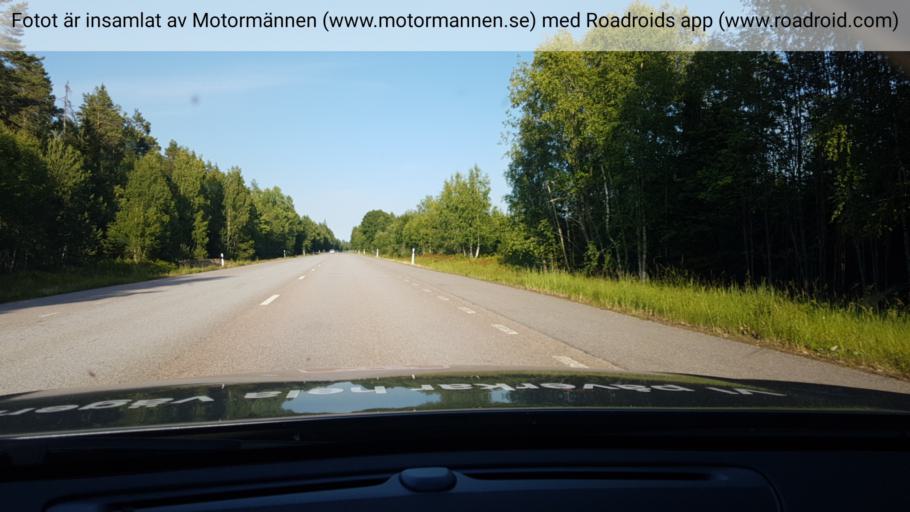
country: SE
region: Uppsala
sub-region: Osthammars Kommun
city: Gimo
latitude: 60.1646
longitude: 18.1213
